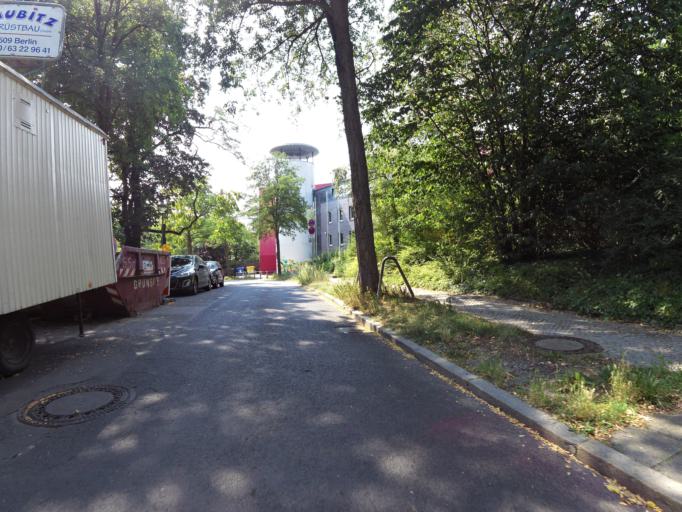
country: DE
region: Berlin
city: Steglitz Bezirk
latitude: 52.4548
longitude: 13.3107
